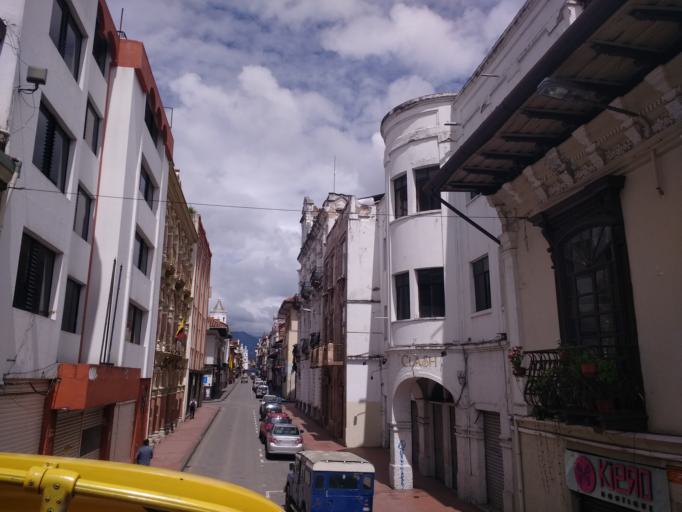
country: EC
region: Azuay
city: Cuenca
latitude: -2.8965
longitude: -79.0061
